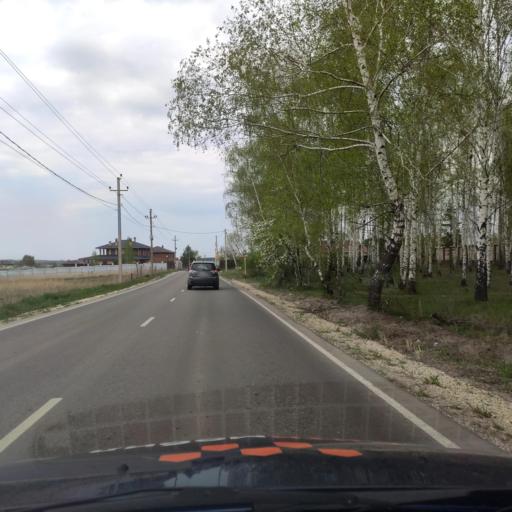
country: RU
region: Voronezj
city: Podgornoye
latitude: 51.8435
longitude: 39.1452
